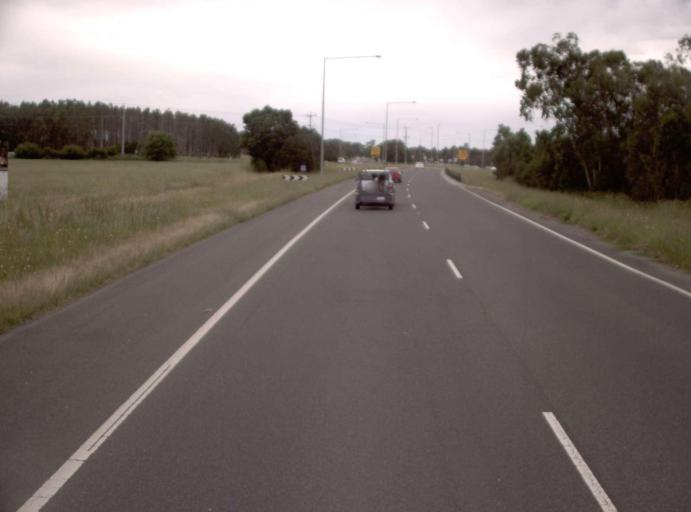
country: AU
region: Victoria
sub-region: Cardinia
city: Koo-Wee-Rup
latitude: -38.2693
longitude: 145.5486
